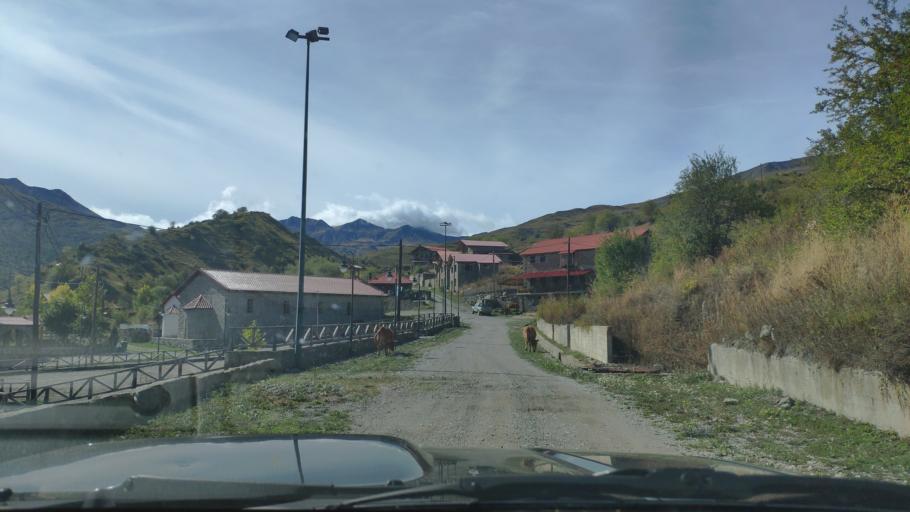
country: AL
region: Korce
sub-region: Rrethi i Devollit
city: Miras
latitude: 40.3919
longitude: 20.8359
